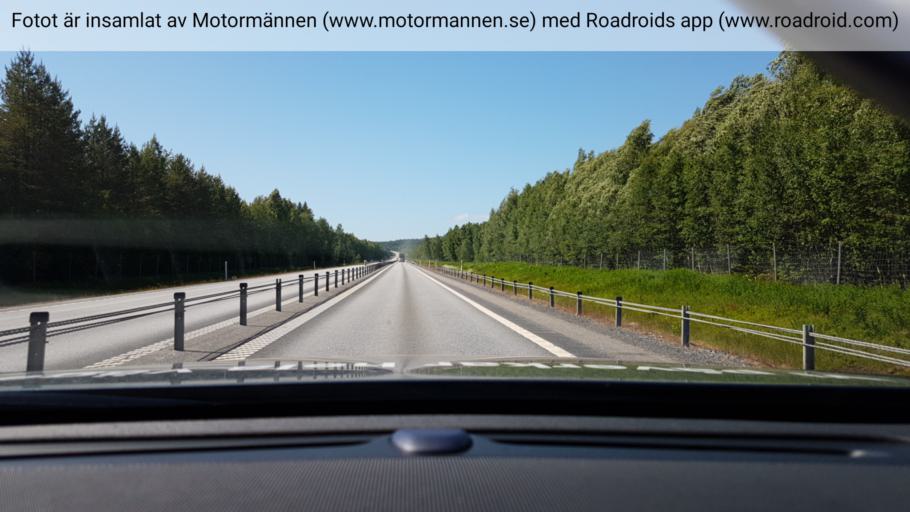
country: SE
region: Vaesterbotten
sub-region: Umea Kommun
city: Roback
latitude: 63.7365
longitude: 20.1080
